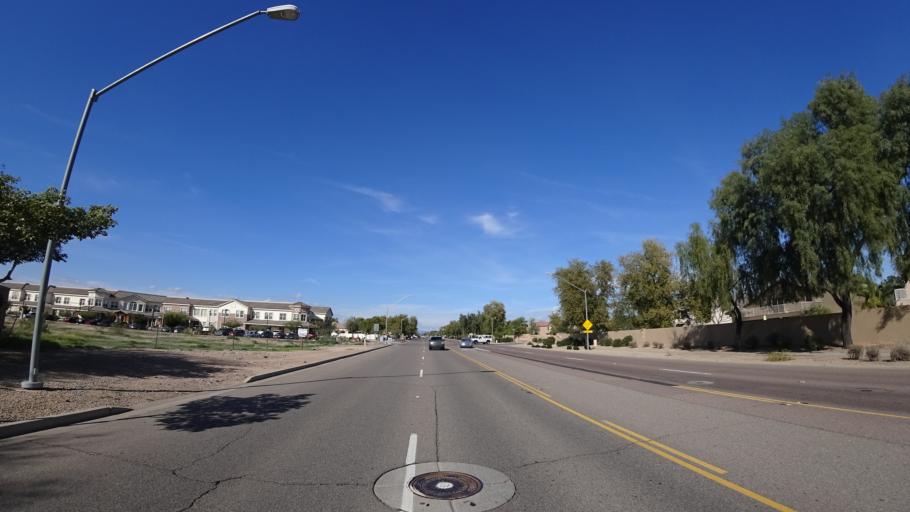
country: US
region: Arizona
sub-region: Maricopa County
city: Sun City
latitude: 33.6780
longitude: -112.2204
